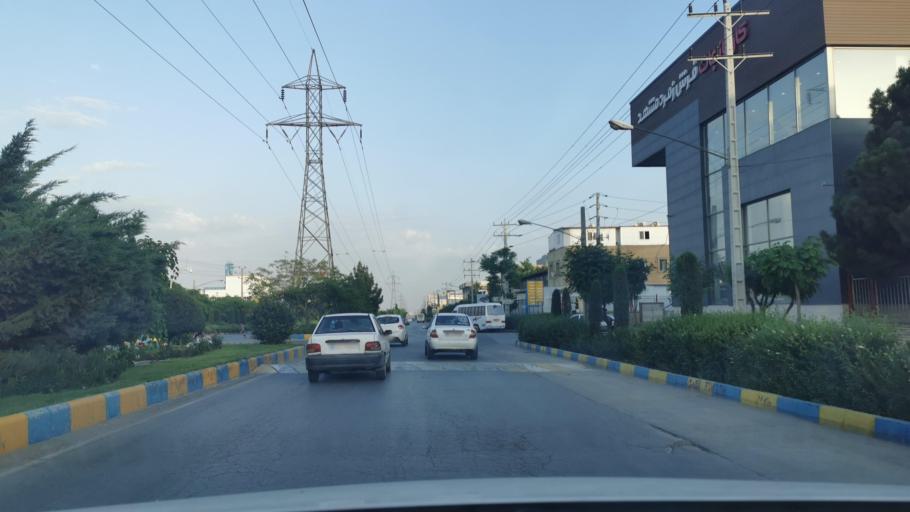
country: IR
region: Razavi Khorasan
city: Torqabeh
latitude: 36.4268
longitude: 59.4217
